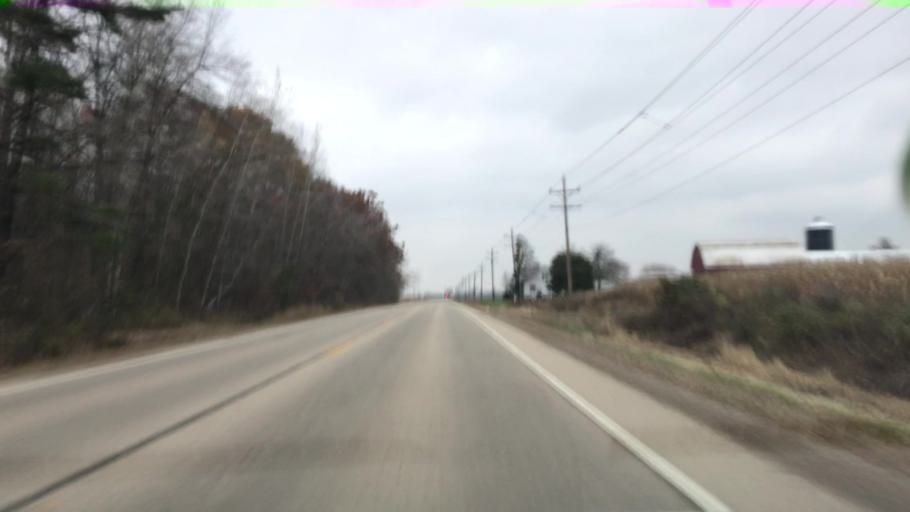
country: US
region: Wisconsin
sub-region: Outagamie County
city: Seymour
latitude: 44.4918
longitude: -88.2911
